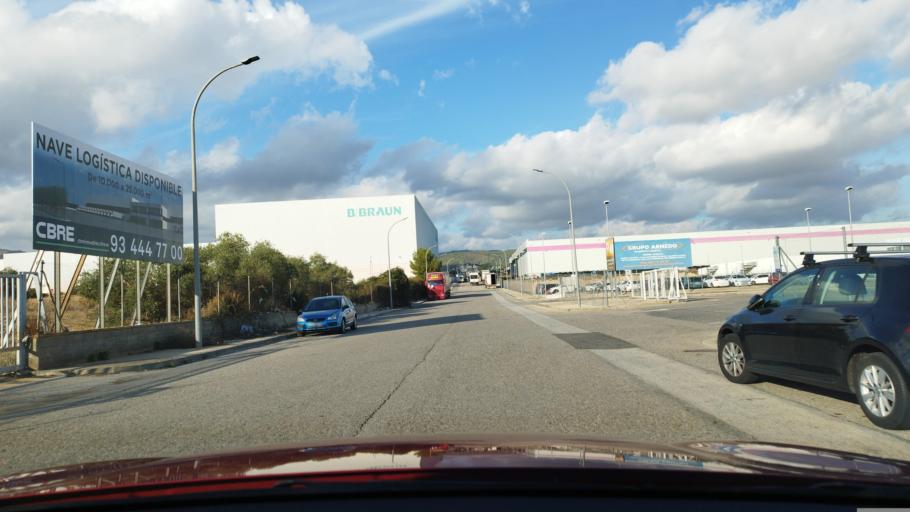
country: ES
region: Catalonia
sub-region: Provincia de Tarragona
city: la Bisbal del Penedes
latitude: 41.2705
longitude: 1.5168
